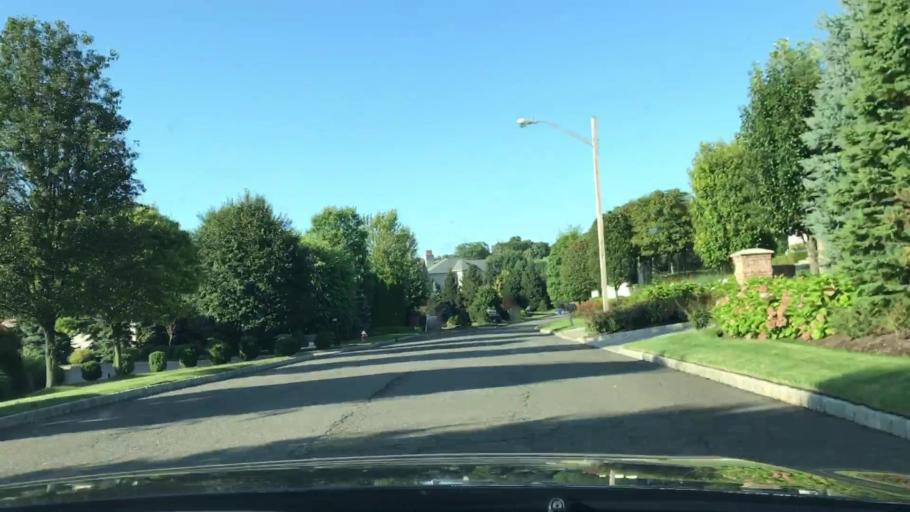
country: US
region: New Jersey
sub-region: Bergen County
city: Tenafly
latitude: 40.9280
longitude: -73.9418
